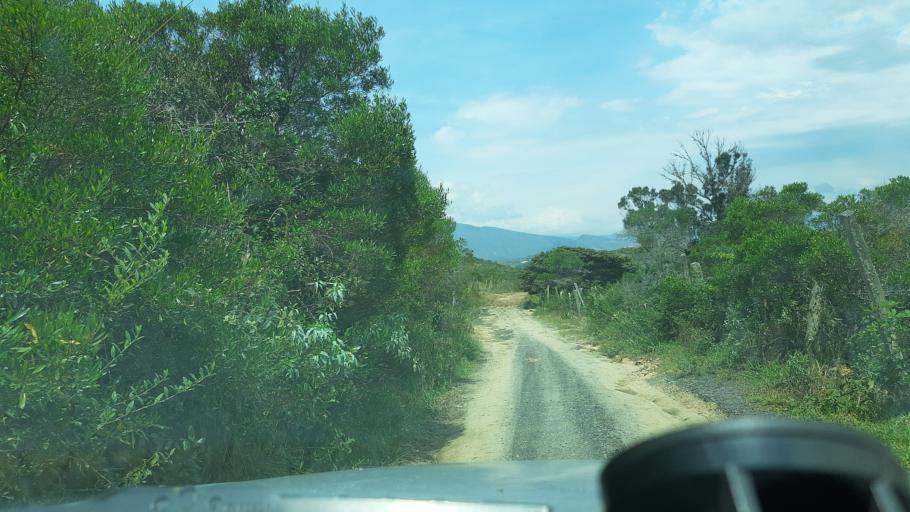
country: CO
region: Boyaca
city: Santa Sofia
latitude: 5.7037
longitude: -73.5823
